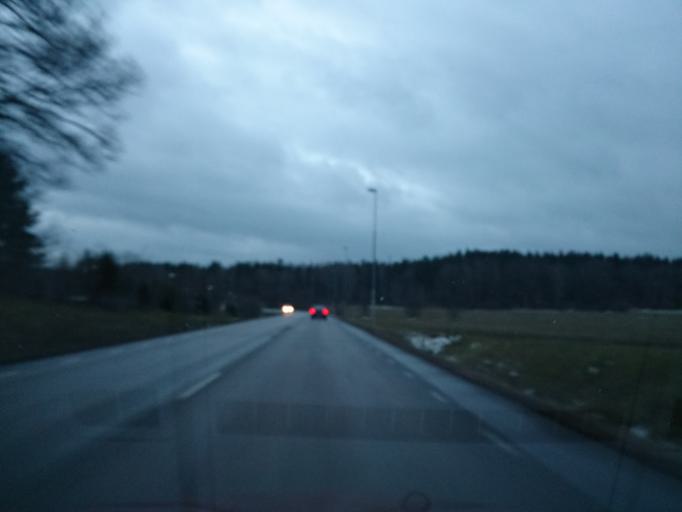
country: SE
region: OEstergoetland
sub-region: Linkopings Kommun
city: Linkoping
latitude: 58.3790
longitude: 15.6351
